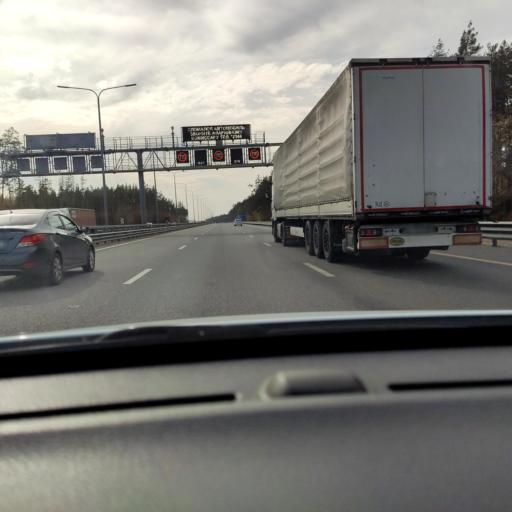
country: RU
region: Voronezj
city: Somovo
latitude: 51.7026
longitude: 39.3053
